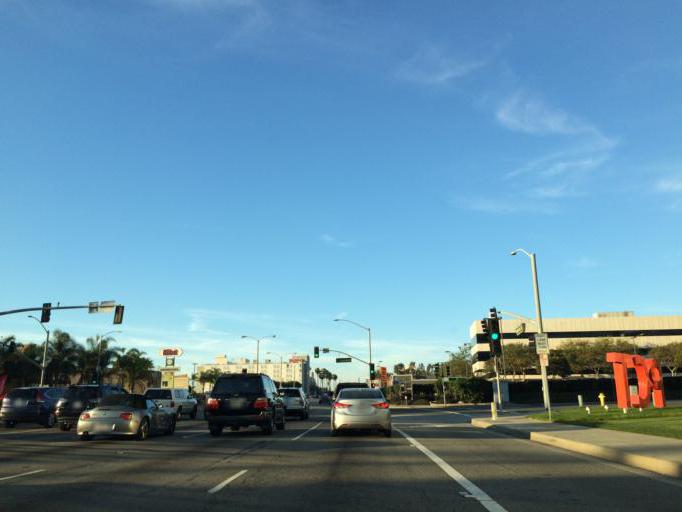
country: US
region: California
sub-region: Los Angeles County
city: El Segundo
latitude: 33.9190
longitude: -118.3958
